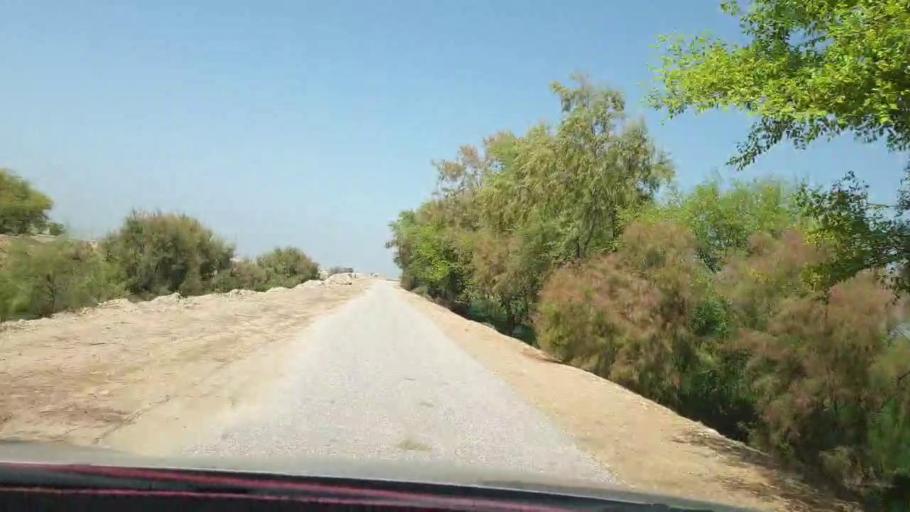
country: PK
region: Sindh
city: Warah
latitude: 27.5604
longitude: 67.7407
